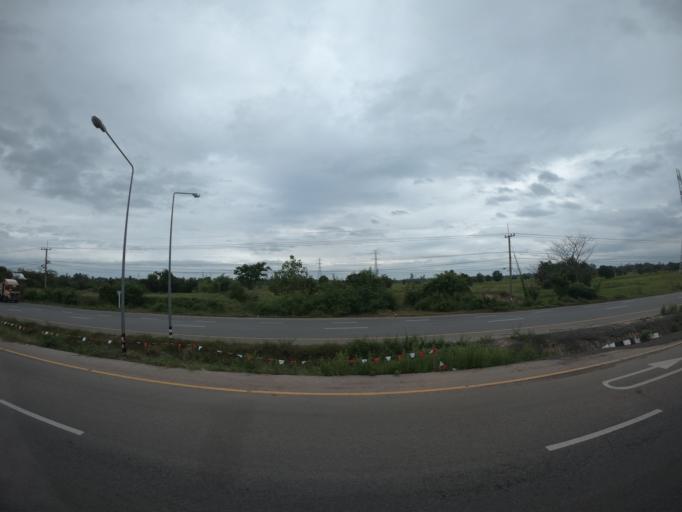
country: TH
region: Roi Et
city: Changhan
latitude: 16.0920
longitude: 103.5459
